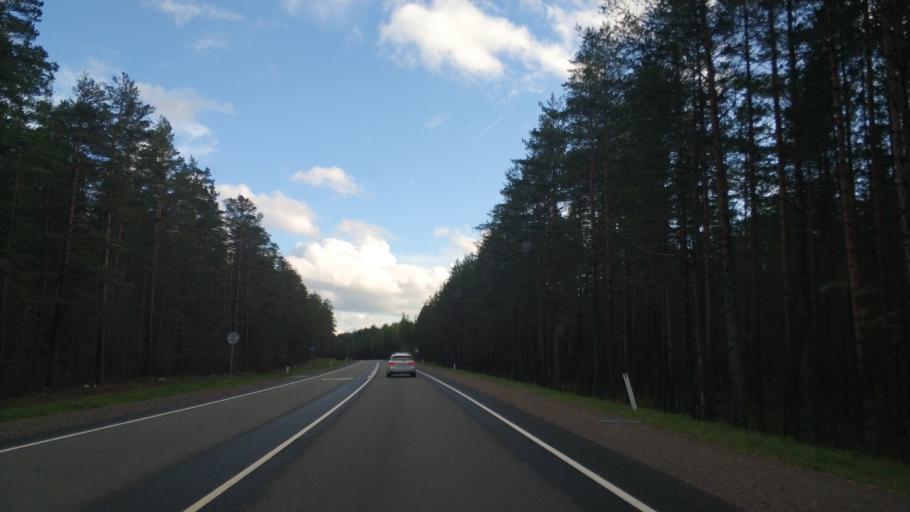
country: RU
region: Leningrad
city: Priozersk
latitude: 60.9875
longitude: 30.1833
